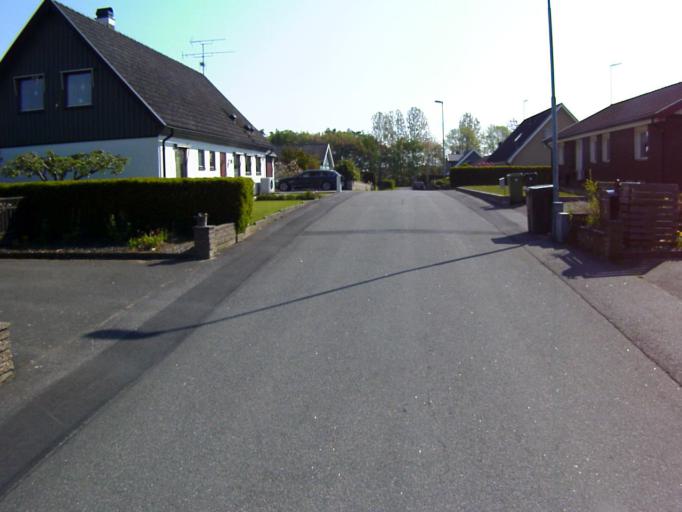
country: SE
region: Skane
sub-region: Kristianstads Kommun
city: Norra Asum
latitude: 55.9486
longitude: 14.1577
